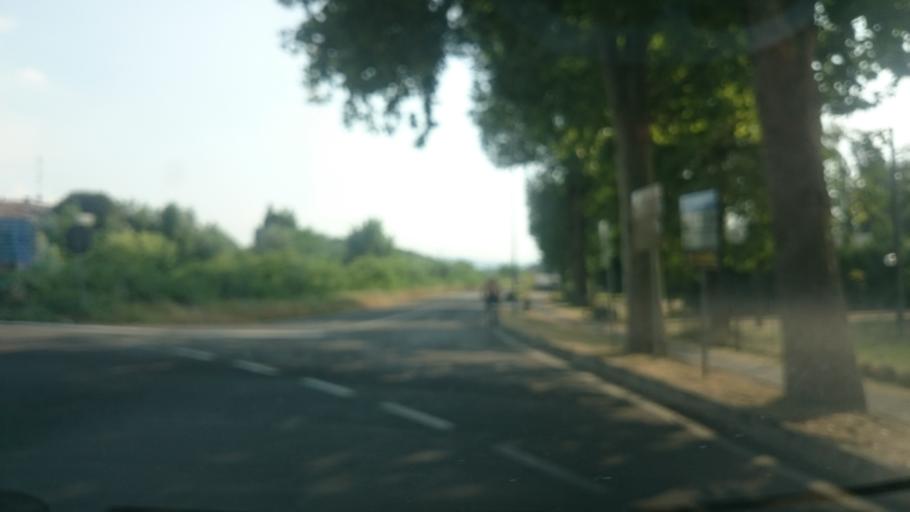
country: IT
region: Emilia-Romagna
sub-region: Provincia di Reggio Emilia
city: Rubiera
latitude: 44.6429
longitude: 10.7799
